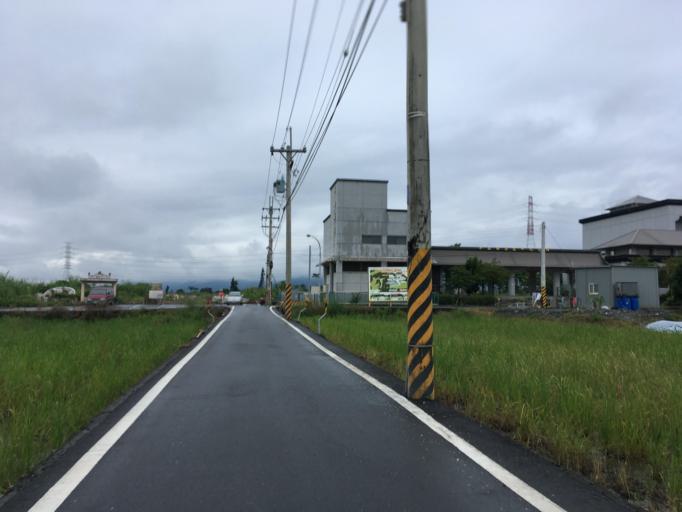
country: TW
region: Taiwan
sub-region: Yilan
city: Yilan
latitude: 24.6635
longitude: 121.7455
